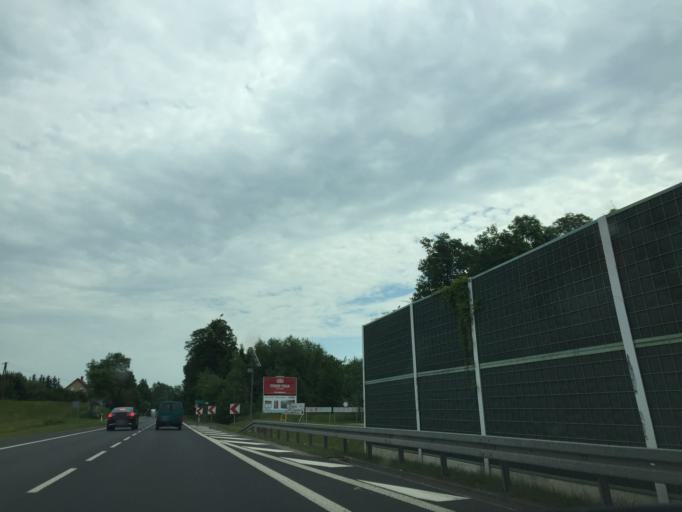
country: PL
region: Warmian-Masurian Voivodeship
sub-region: Powiat mragowski
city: Mragowo
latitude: 53.8812
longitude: 21.3474
